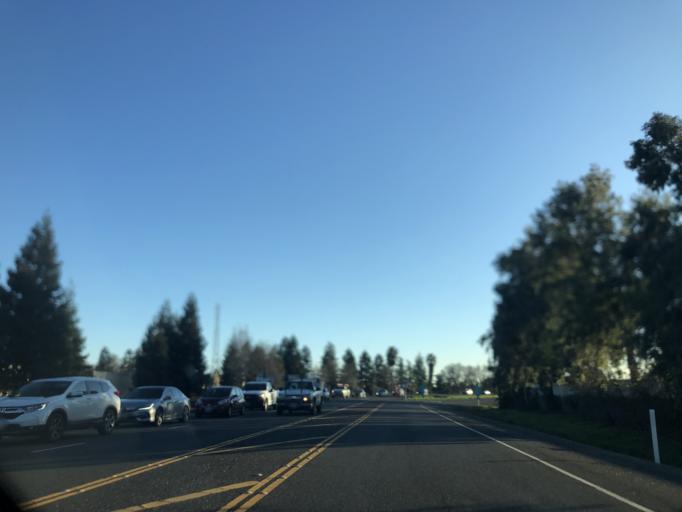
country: US
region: California
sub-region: Yolo County
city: Woodland
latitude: 38.6756
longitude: -121.7496
